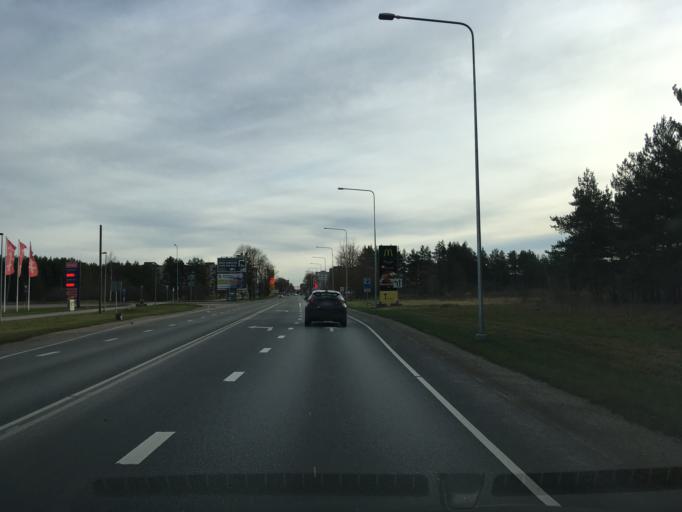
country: EE
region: Ida-Virumaa
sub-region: Narva linn
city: Narva
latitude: 59.3856
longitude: 28.1531
